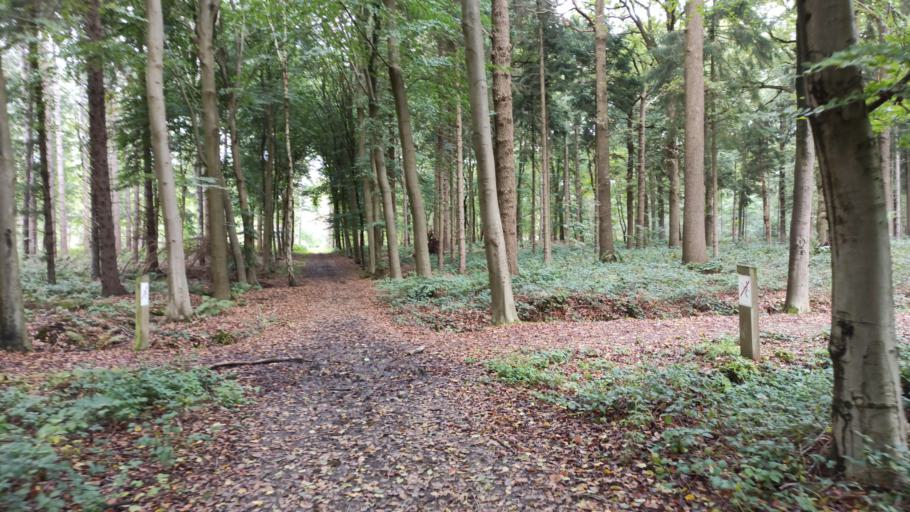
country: BE
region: Flanders
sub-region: Provincie West-Vlaanderen
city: Ruiselede
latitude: 51.0843
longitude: 3.3916
